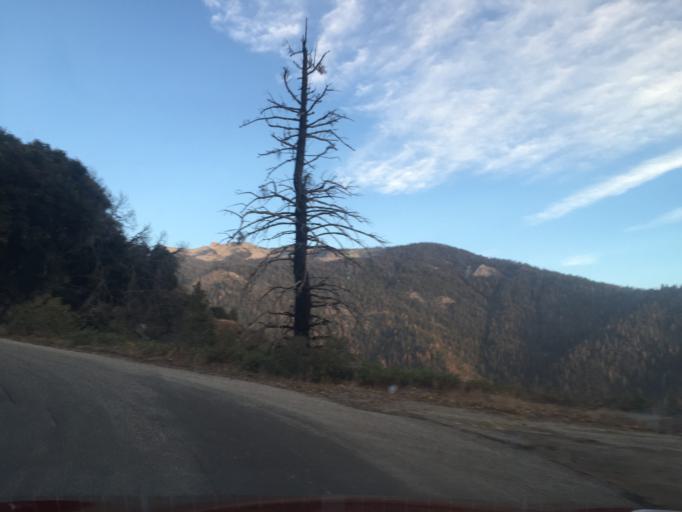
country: US
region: California
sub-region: Tulare County
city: Three Rivers
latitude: 36.4515
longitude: -118.6999
